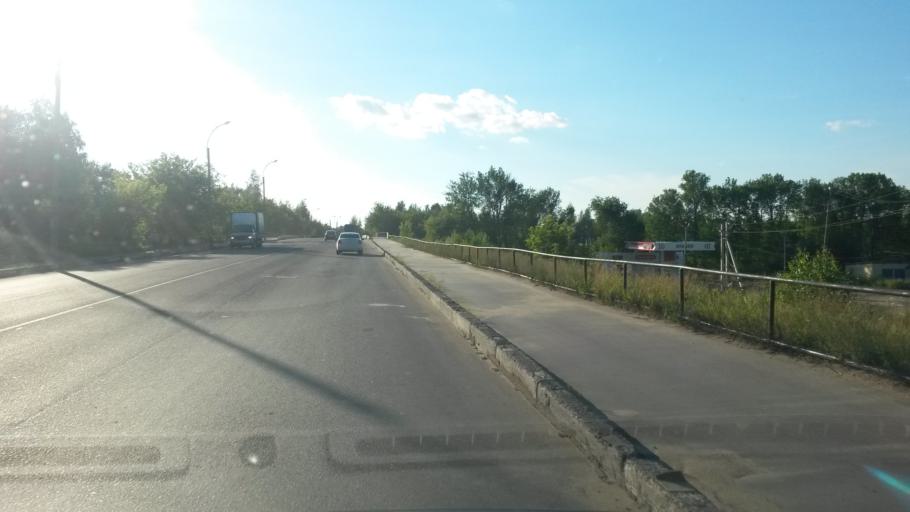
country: RU
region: Ivanovo
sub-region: Gorod Ivanovo
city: Ivanovo
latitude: 57.0166
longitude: 40.9275
